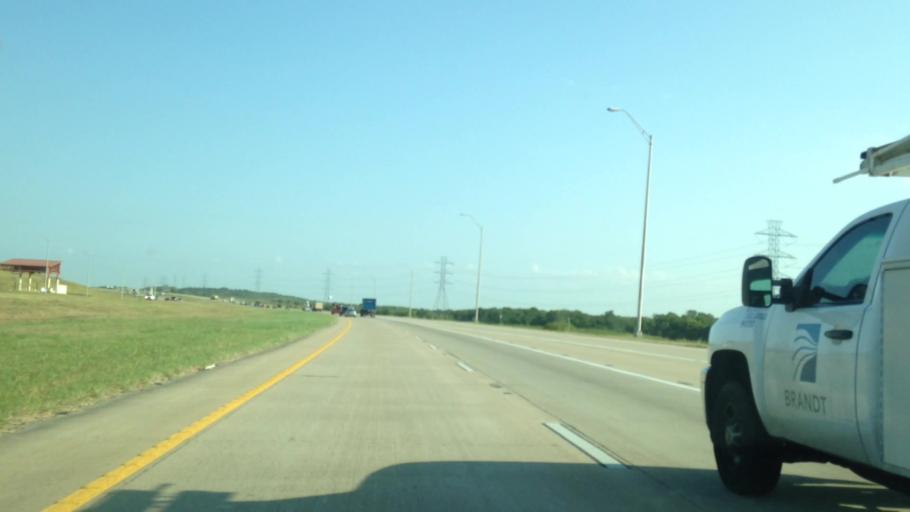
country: US
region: Texas
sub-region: Travis County
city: Manor
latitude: 30.3039
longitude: -97.5690
